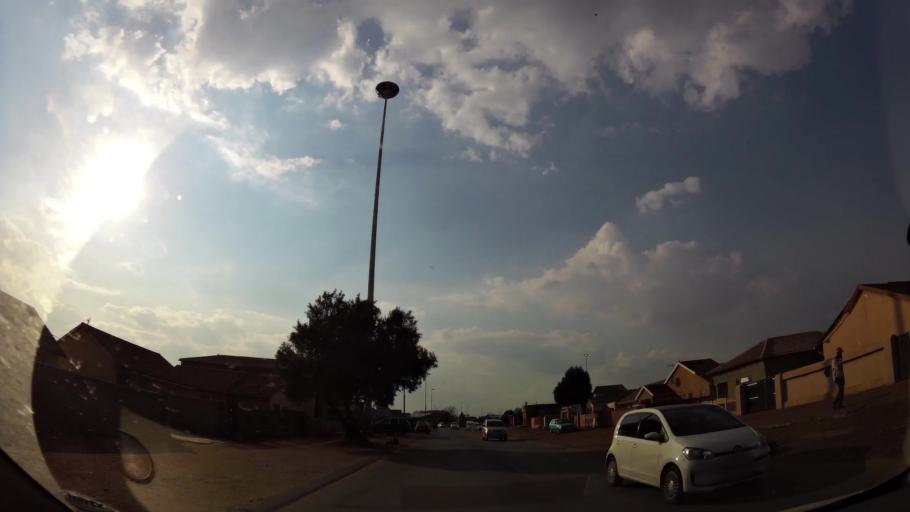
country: ZA
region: Gauteng
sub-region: Ekurhuleni Metropolitan Municipality
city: Germiston
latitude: -26.3596
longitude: 28.2076
